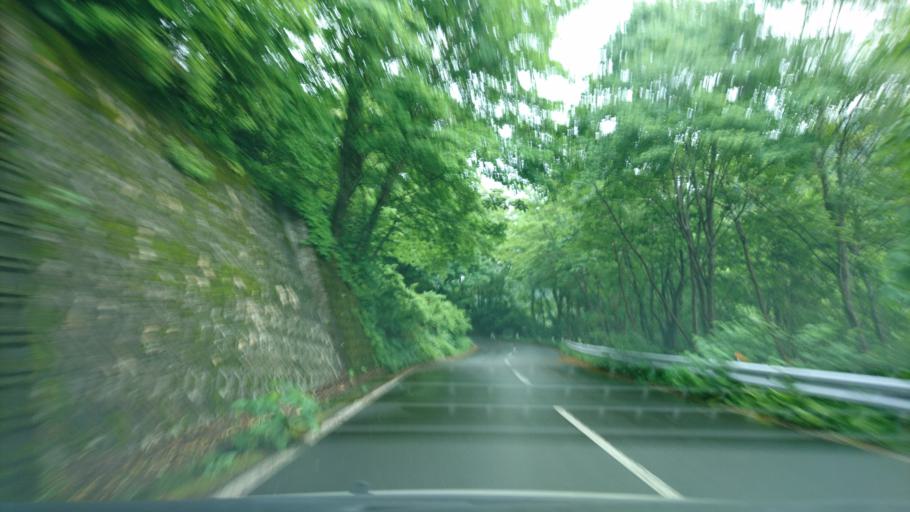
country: JP
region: Iwate
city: Ichinoseki
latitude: 39.0051
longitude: 140.8442
